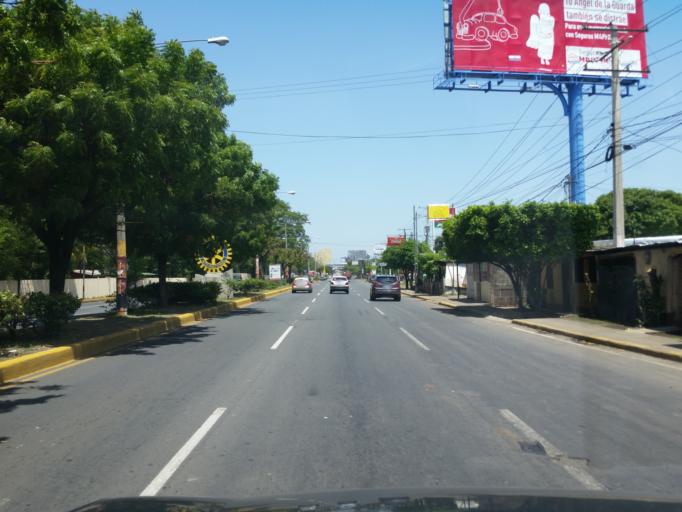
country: NI
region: Managua
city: Managua
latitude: 12.1461
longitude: -86.1764
